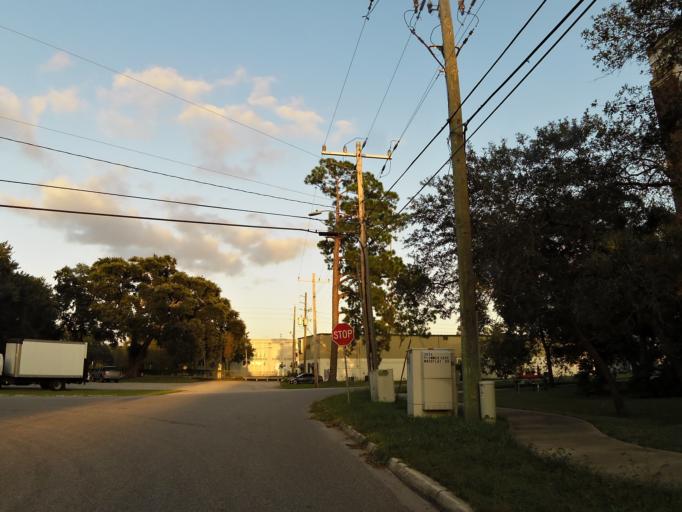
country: US
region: Florida
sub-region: Saint Johns County
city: Fruit Cove
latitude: 30.1797
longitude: -81.6295
